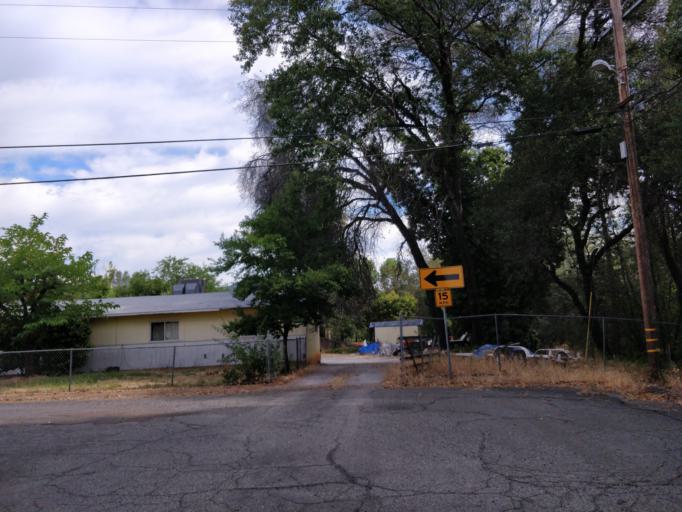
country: US
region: California
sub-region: Shasta County
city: Shasta Lake
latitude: 40.6848
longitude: -122.3567
